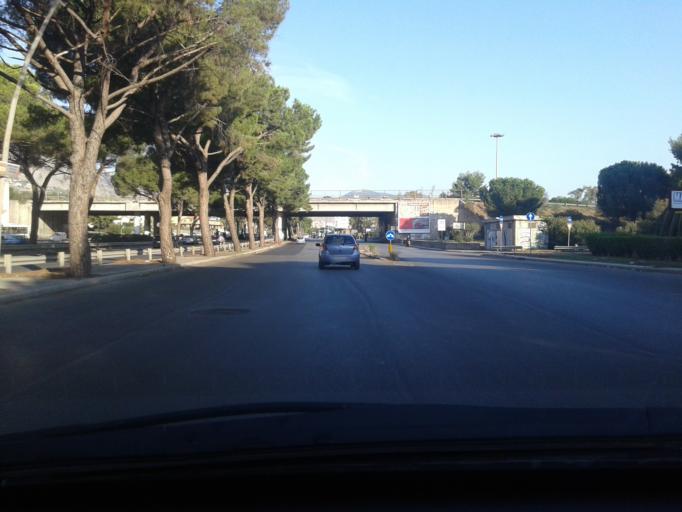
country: IT
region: Sicily
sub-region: Palermo
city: Villa Ciambra
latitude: 38.0931
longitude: 13.3405
